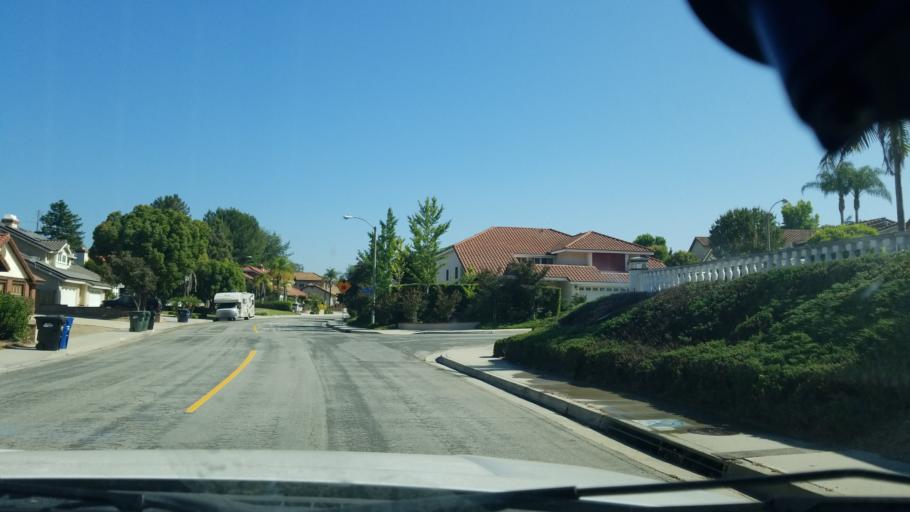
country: US
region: California
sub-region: Los Angeles County
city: Rowland Heights
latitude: 33.9798
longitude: -117.9257
